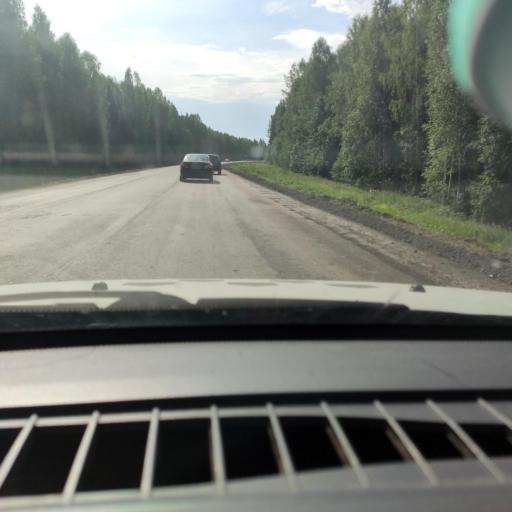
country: RU
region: Perm
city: Siva
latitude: 58.4793
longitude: 54.3987
